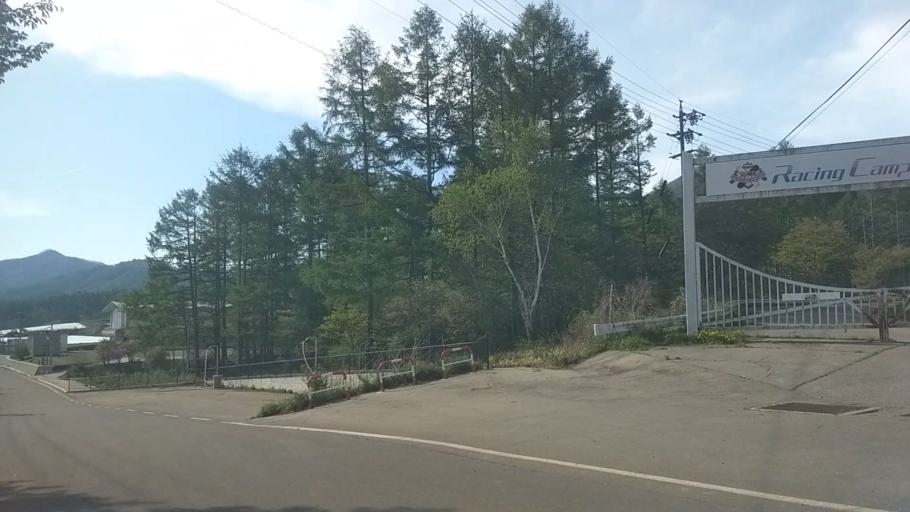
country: JP
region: Yamanashi
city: Nirasaki
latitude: 35.9372
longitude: 138.4655
